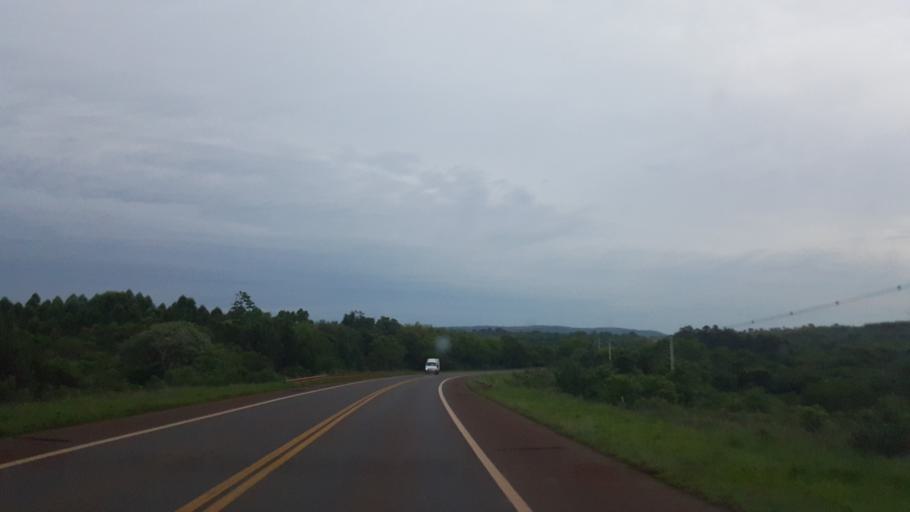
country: AR
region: Misiones
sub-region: Departamento de Apostoles
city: San Jose
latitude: -27.7669
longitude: -55.8018
